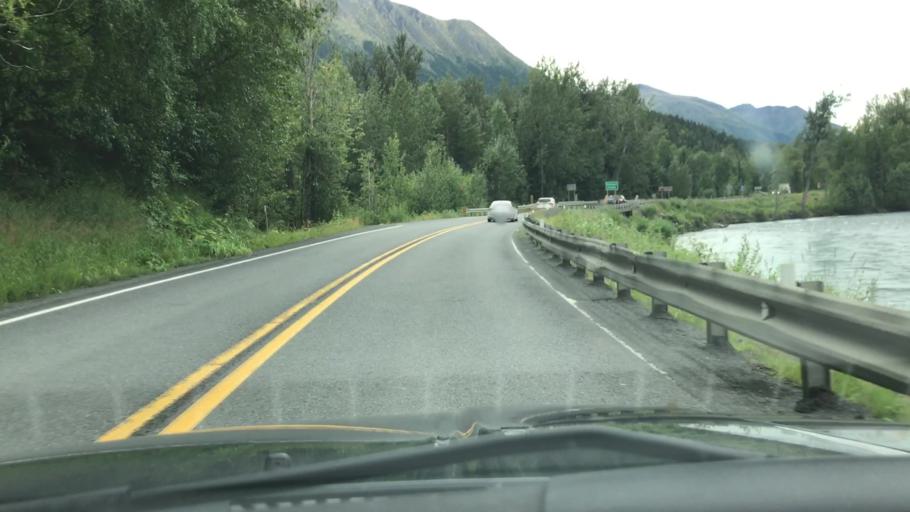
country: US
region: Alaska
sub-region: Kenai Peninsula Borough
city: Seward
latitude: 60.4845
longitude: -149.8790
